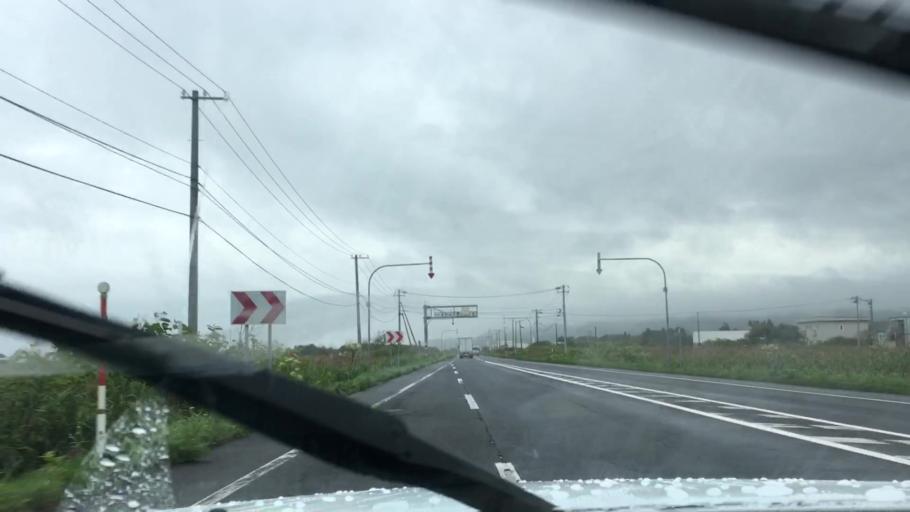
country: JP
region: Hokkaido
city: Niseko Town
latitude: 42.3973
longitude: 140.3015
